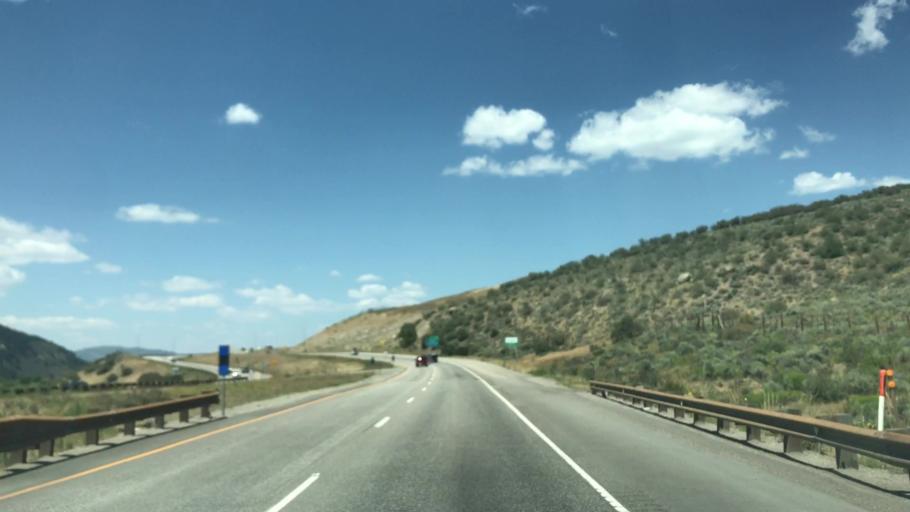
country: US
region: Colorado
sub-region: Eagle County
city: Avon
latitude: 39.6236
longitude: -106.4858
